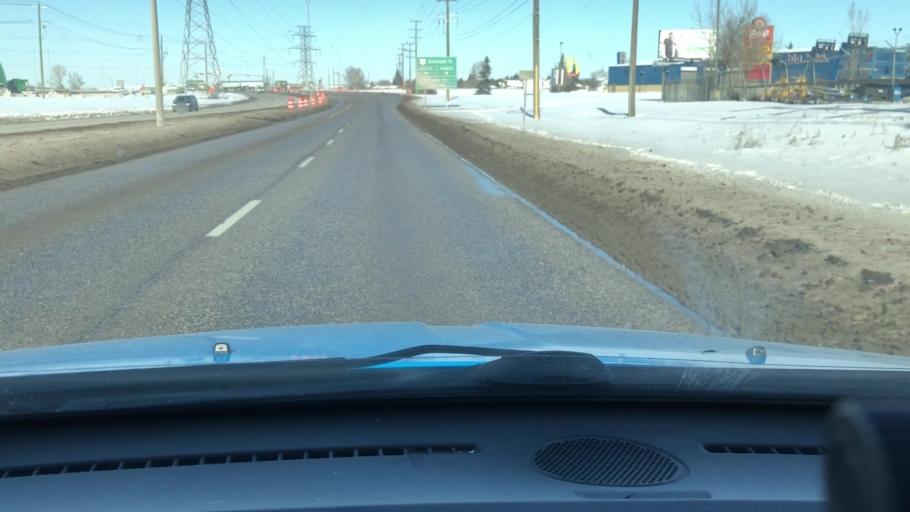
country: CA
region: Alberta
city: Calgary
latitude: 51.0120
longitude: -114.0016
